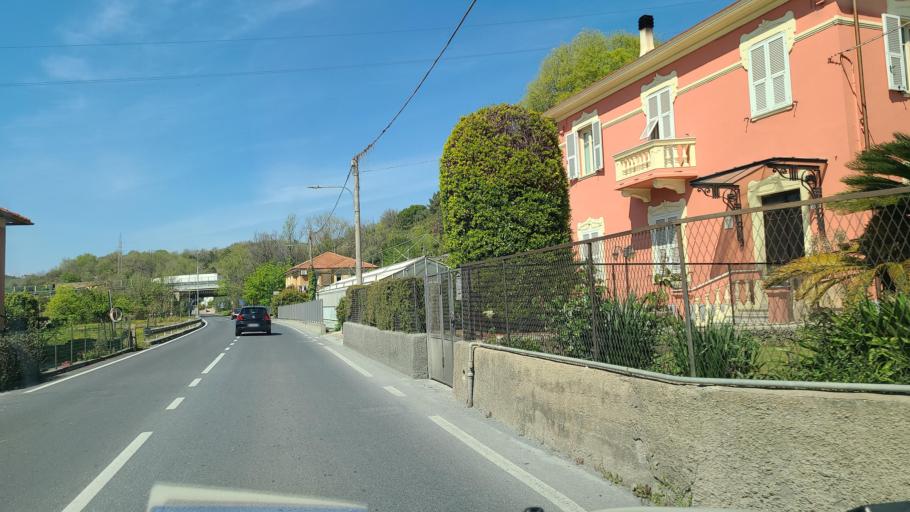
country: IT
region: Liguria
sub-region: Provincia di Savona
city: San Fedele-Lusignano
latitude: 44.0570
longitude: 8.1689
